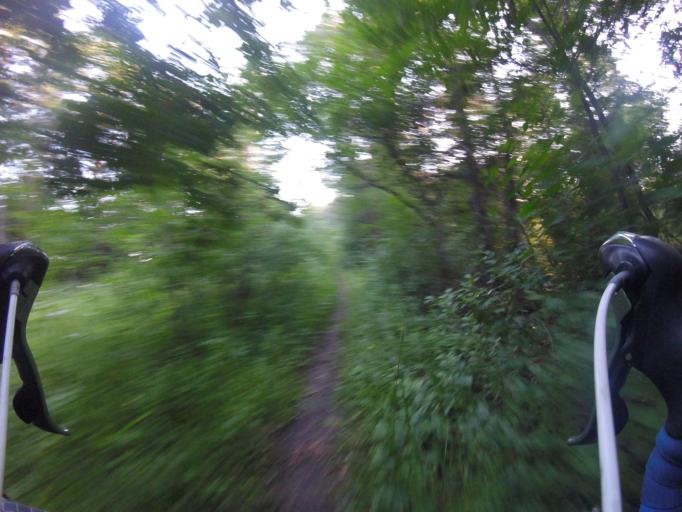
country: CA
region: Ontario
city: Bells Corners
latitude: 45.3560
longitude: -75.8552
